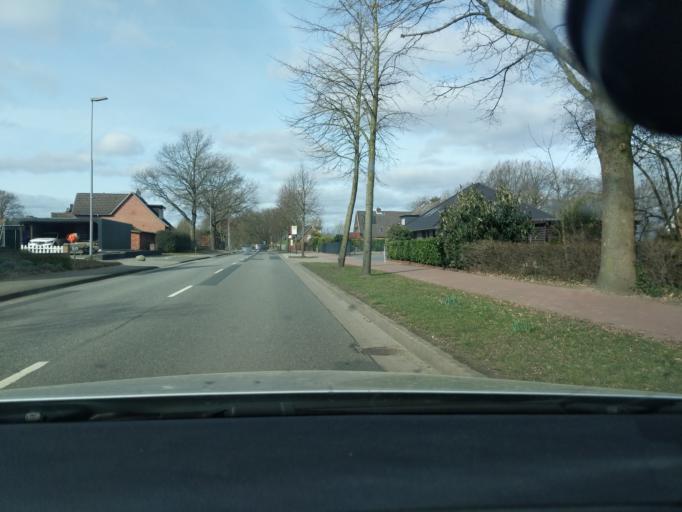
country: DE
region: Lower Saxony
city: Agathenburg
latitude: 53.5644
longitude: 9.5278
